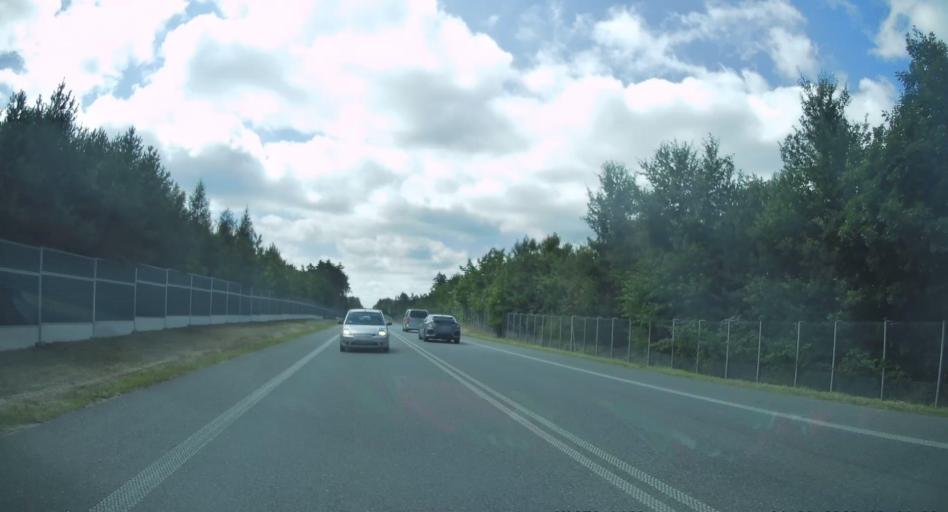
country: PL
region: Subcarpathian Voivodeship
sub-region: Powiat mielecki
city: Mielec
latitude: 50.3106
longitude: 21.5024
